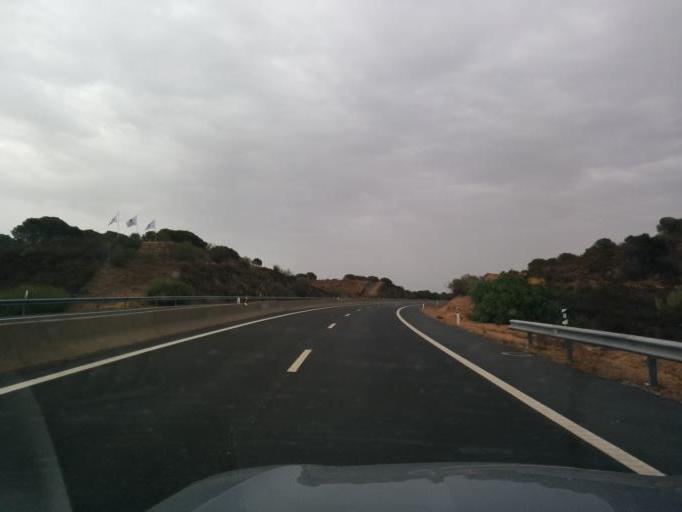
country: PT
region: Faro
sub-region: Castro Marim
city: Castro Marim
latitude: 37.2283
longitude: -7.4688
